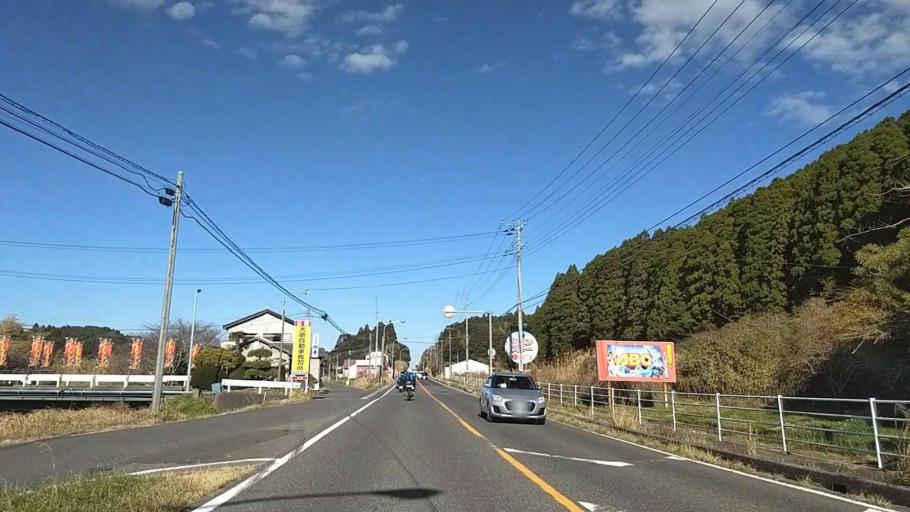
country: JP
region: Chiba
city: Ohara
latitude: 35.2123
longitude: 140.3759
